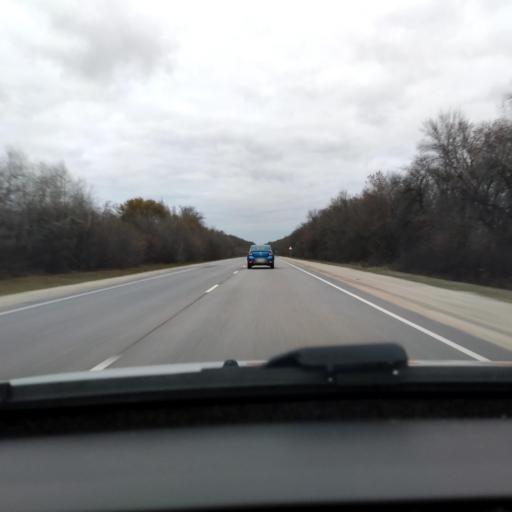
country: RU
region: Lipetsk
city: Borinskoye
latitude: 52.3808
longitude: 39.2189
